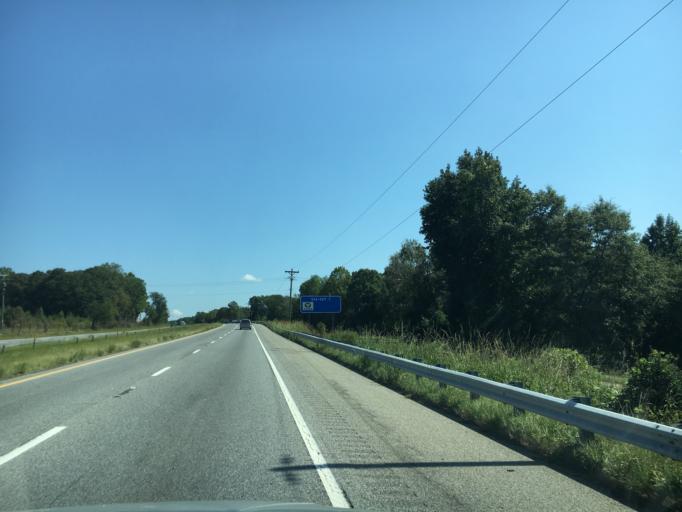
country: US
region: South Carolina
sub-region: Spartanburg County
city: Valley Falls
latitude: 34.9992
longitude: -81.9336
